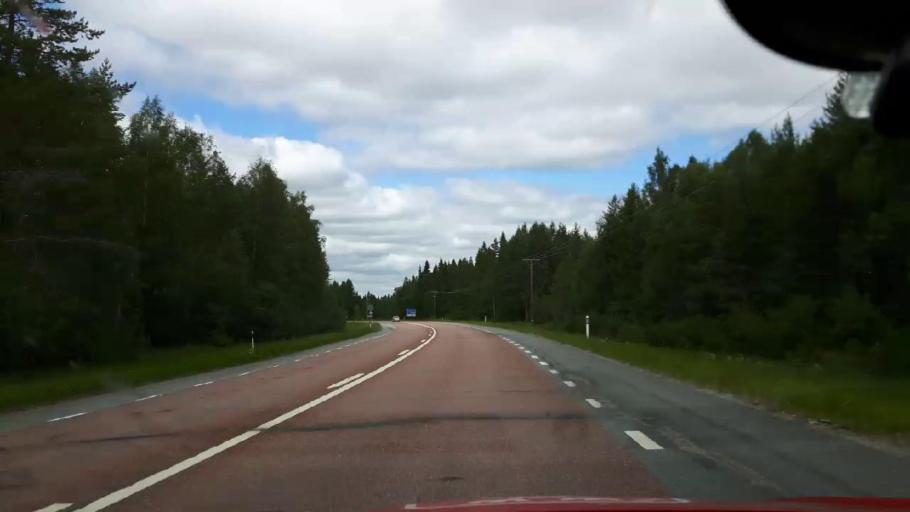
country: SE
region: Jaemtland
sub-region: Braecke Kommun
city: Braecke
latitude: 62.8128
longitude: 15.3613
